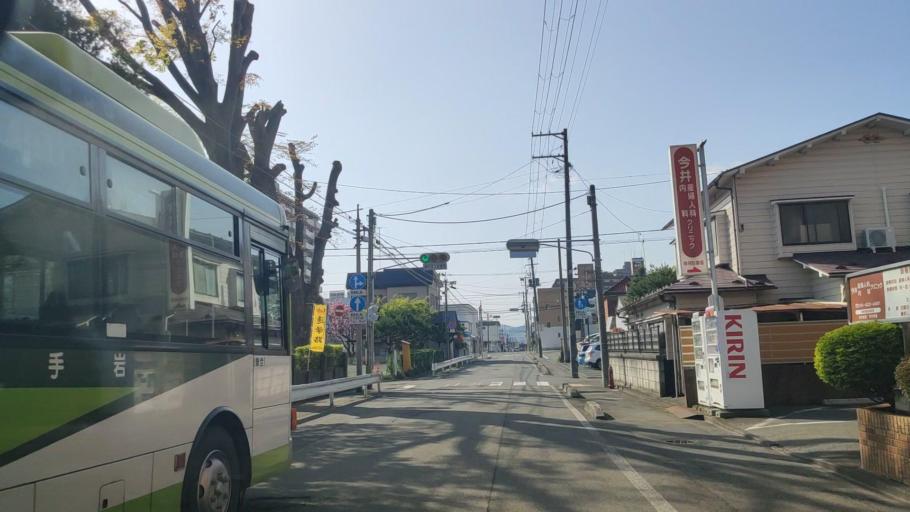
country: JP
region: Iwate
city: Morioka-shi
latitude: 39.6984
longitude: 141.1517
